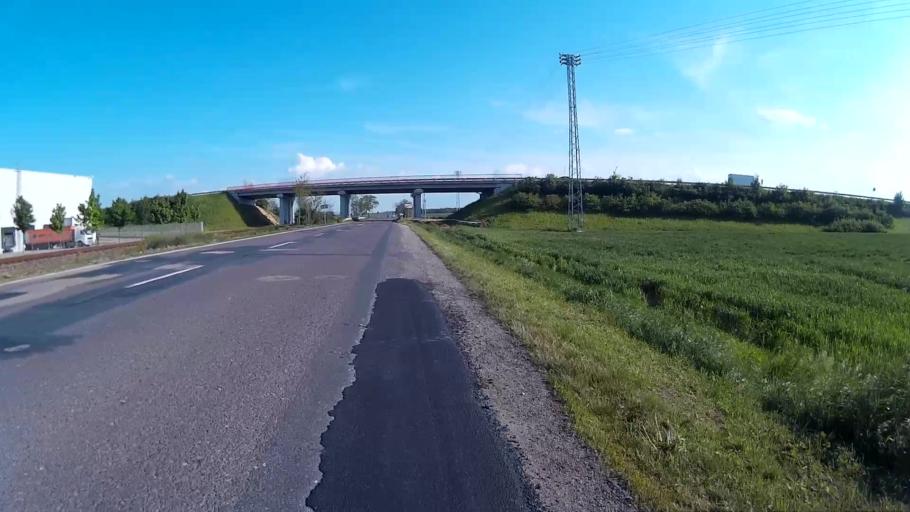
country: CZ
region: South Moravian
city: Pohorelice
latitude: 48.9705
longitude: 16.5173
